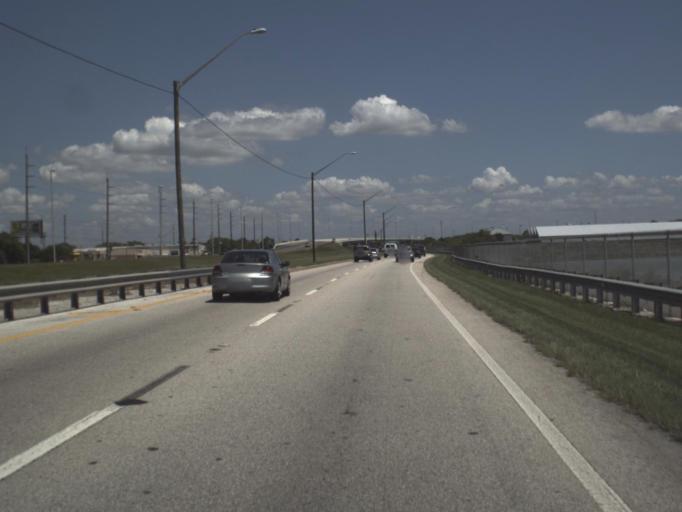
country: US
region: Florida
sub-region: Pinellas County
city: Pinellas Park
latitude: 27.8788
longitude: -82.6861
